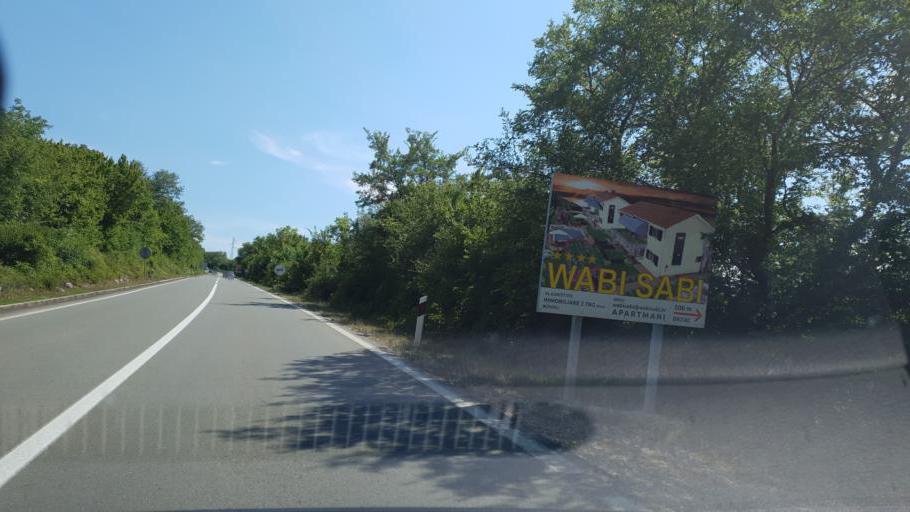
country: HR
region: Primorsko-Goranska
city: Njivice
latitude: 45.0989
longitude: 14.5370
